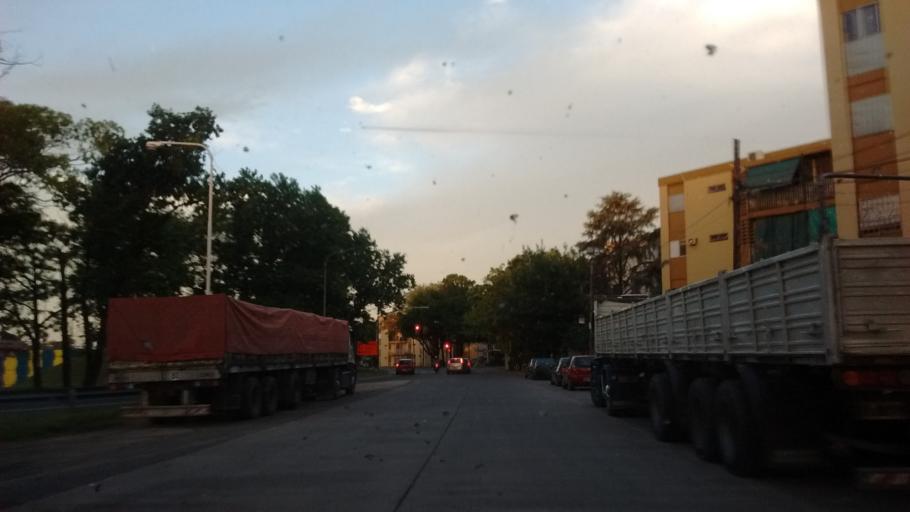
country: AR
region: Santa Fe
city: Granadero Baigorria
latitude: -32.8889
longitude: -60.7151
